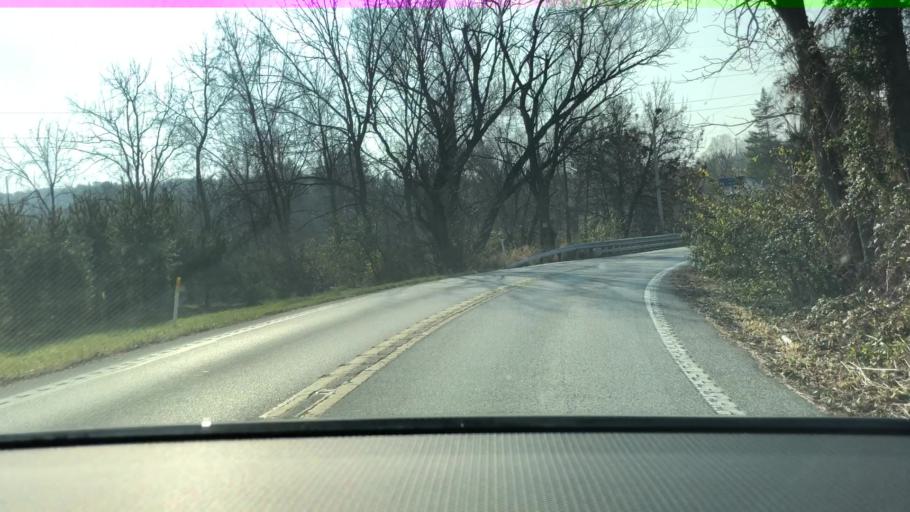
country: US
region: Pennsylvania
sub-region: York County
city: Yoe
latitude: 39.9330
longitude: -76.6556
